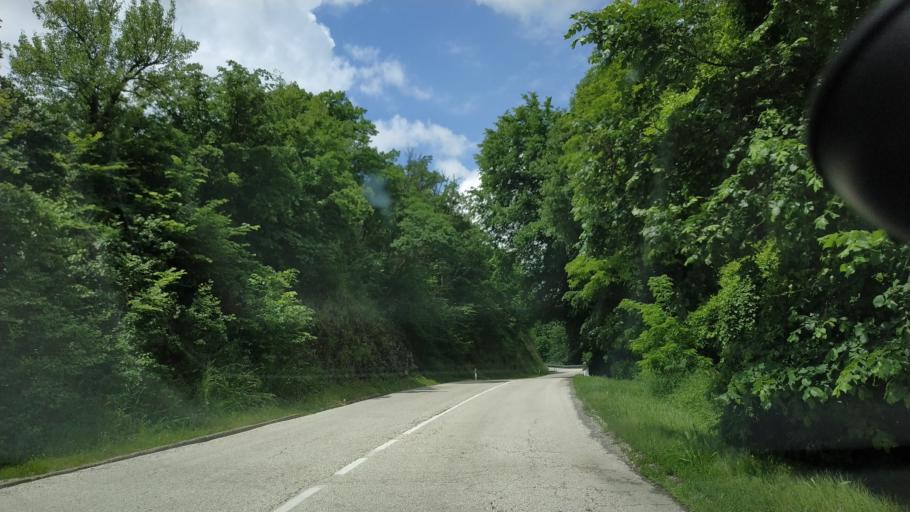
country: RS
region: Central Serbia
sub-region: Borski Okrug
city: Bor
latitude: 44.0610
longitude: 22.0437
